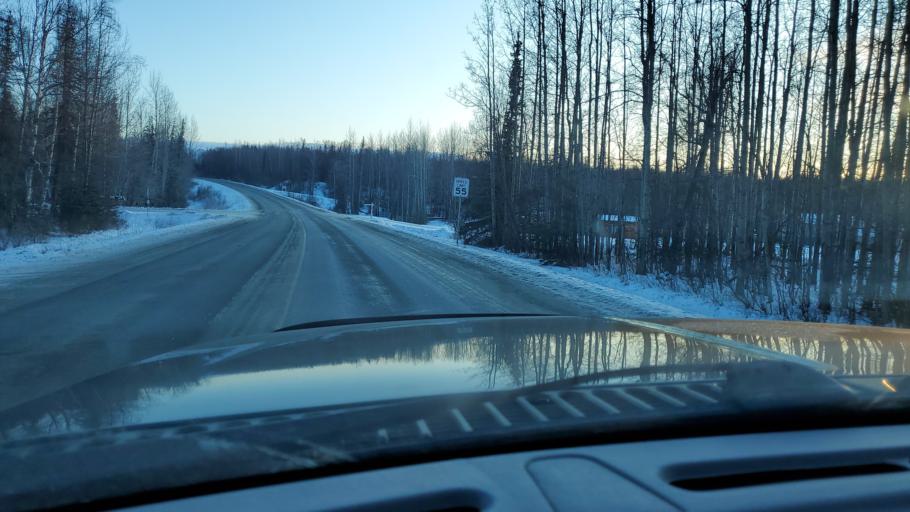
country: US
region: Alaska
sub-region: Matanuska-Susitna Borough
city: Fishhook
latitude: 61.6839
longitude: -149.2394
